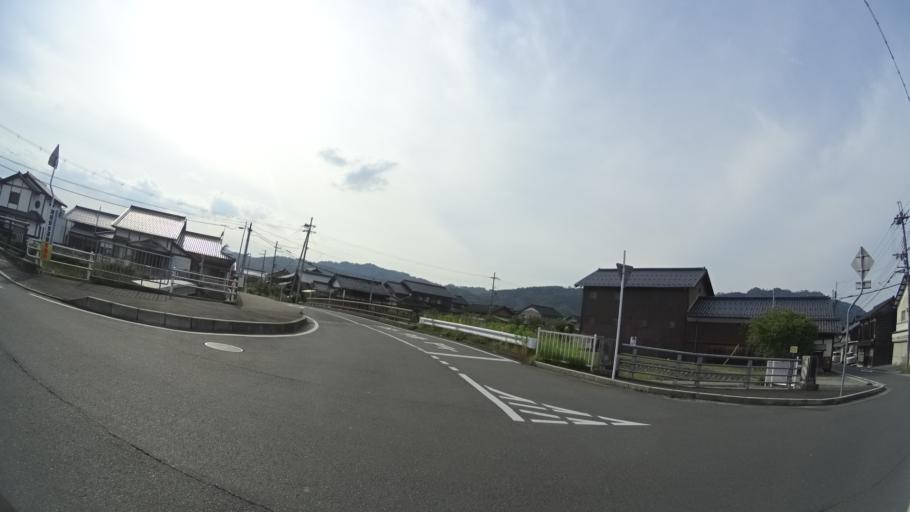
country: JP
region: Kyoto
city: Miyazu
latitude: 35.5312
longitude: 135.1248
